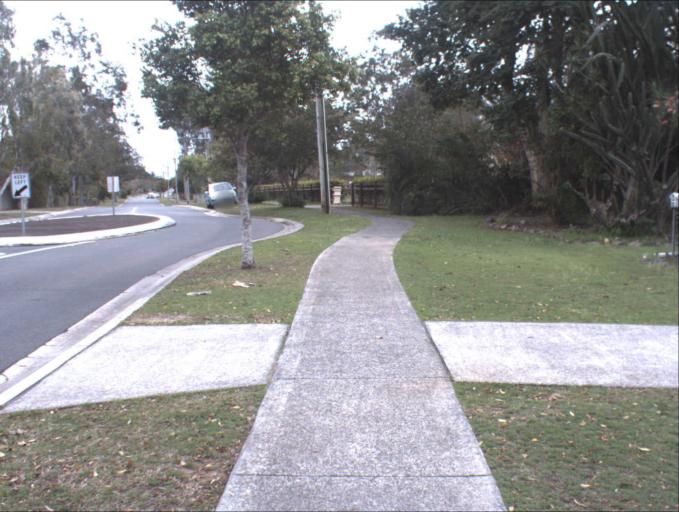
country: AU
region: Queensland
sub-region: Logan
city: Waterford West
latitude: -27.7013
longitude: 153.1374
